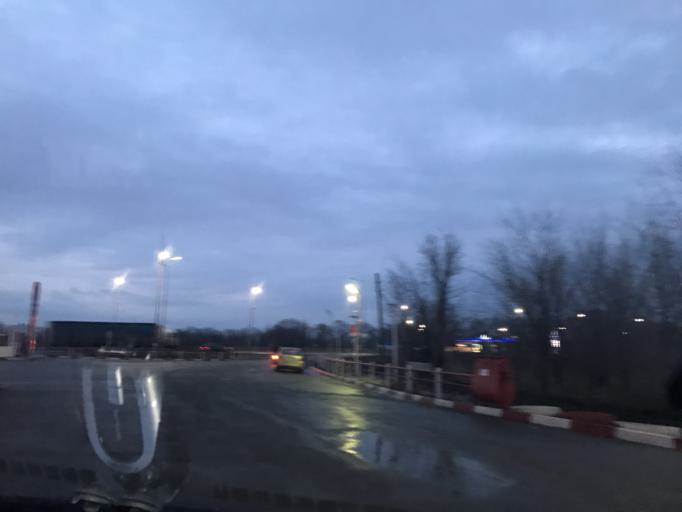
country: RU
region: Rostov
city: Samarskoye
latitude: 46.8739
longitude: 39.7020
